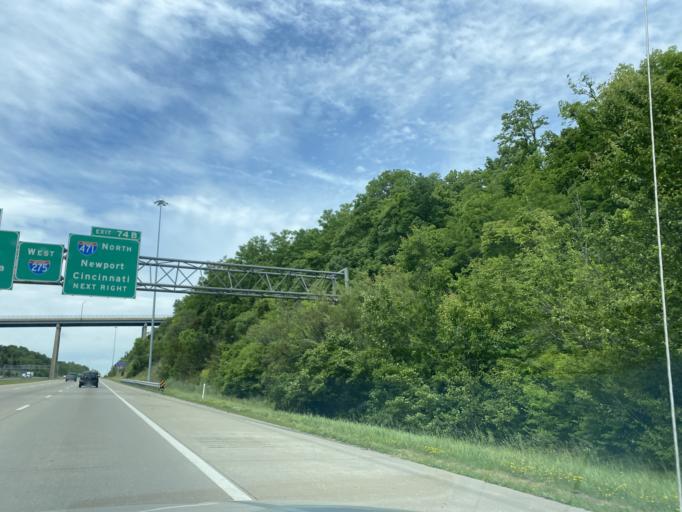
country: US
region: Kentucky
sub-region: Campbell County
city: Highland Heights
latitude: 39.0519
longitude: -84.4431
